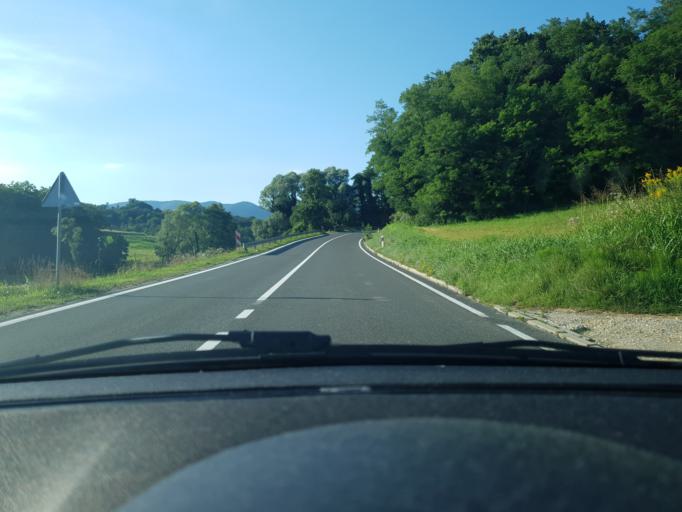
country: HR
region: Krapinsko-Zagorska
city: Radoboj
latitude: 46.1437
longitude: 15.9399
